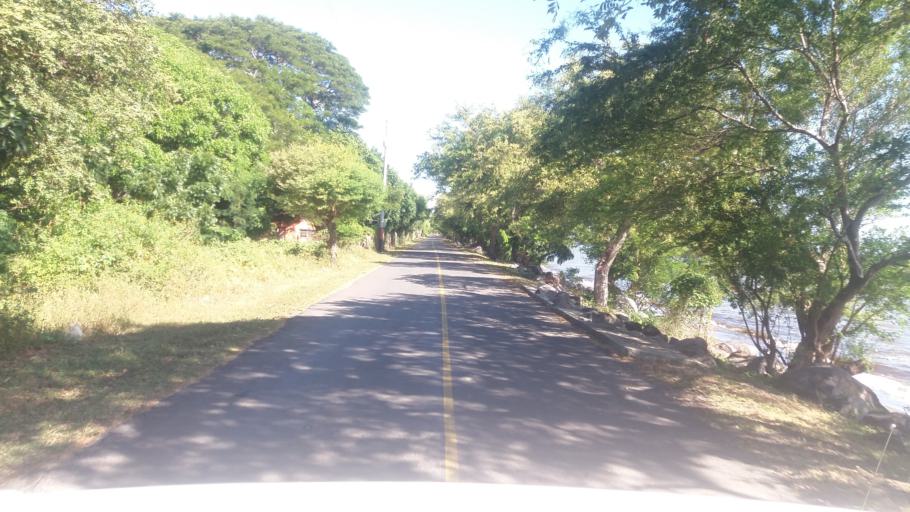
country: NI
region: Granada
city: Granada
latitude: 11.9774
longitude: -85.9417
